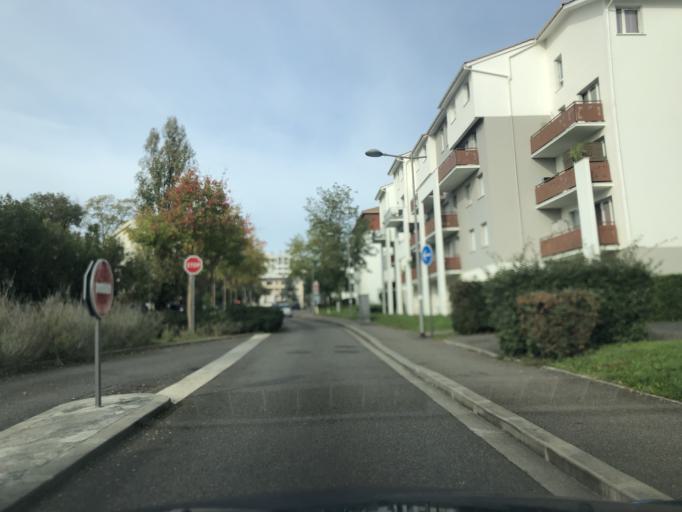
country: FR
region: Aquitaine
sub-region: Departement de la Gironde
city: Merignac
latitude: 44.8431
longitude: -0.6485
